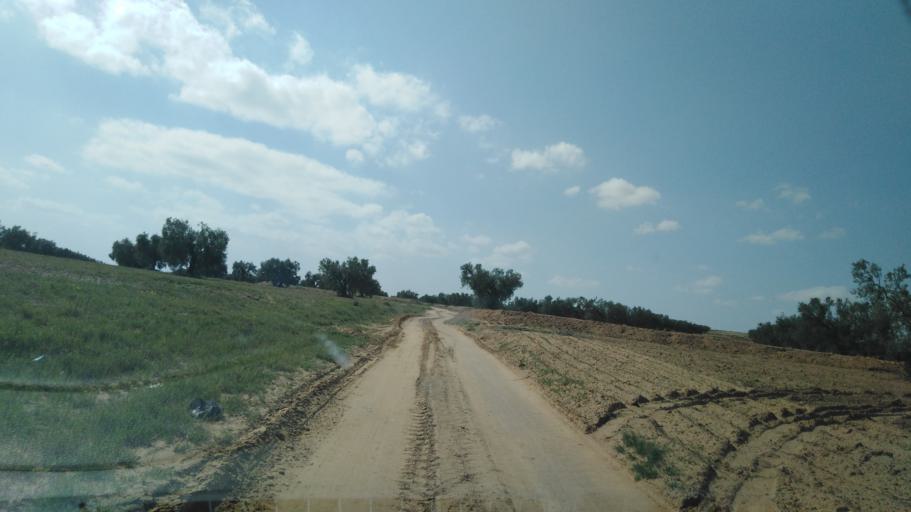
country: TN
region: Safaqis
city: Bi'r `Ali Bin Khalifah
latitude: 34.7928
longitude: 10.3990
